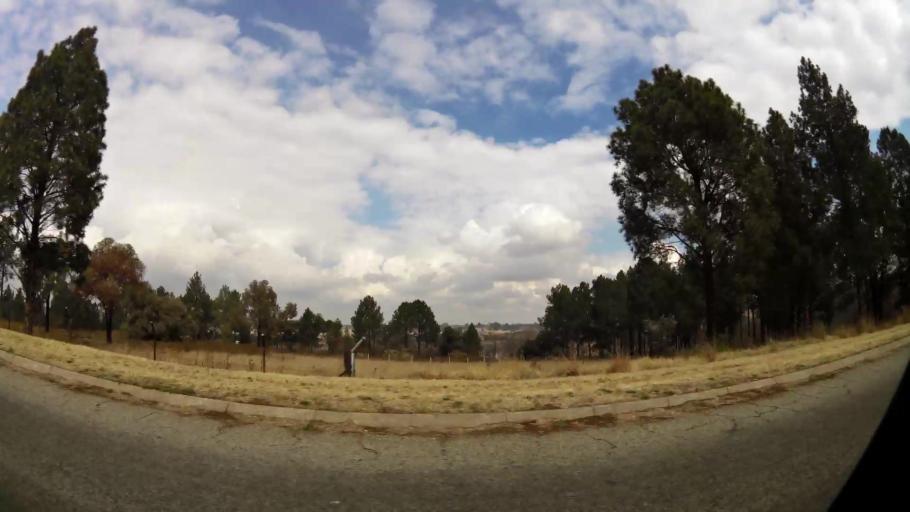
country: ZA
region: Gauteng
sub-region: Sedibeng District Municipality
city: Vanderbijlpark
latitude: -26.7433
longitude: 27.8464
